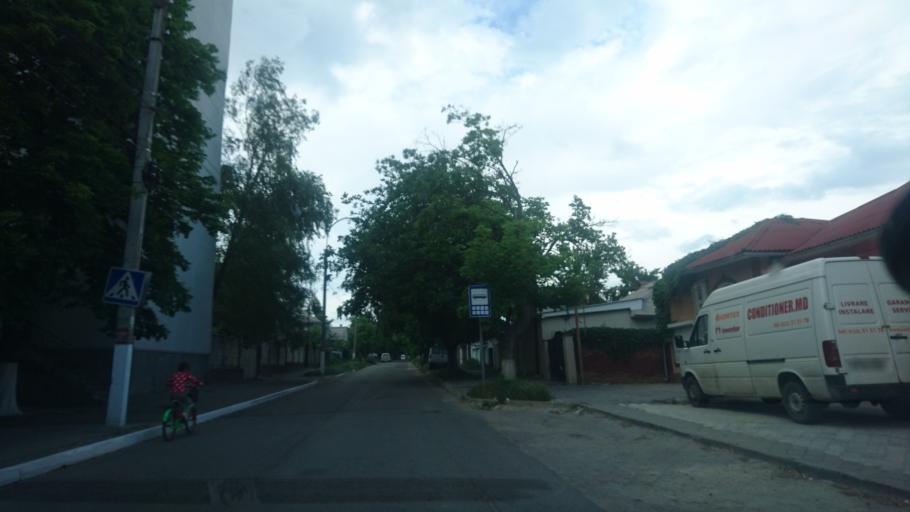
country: MD
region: Chisinau
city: Chisinau
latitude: 47.0496
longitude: 28.8464
